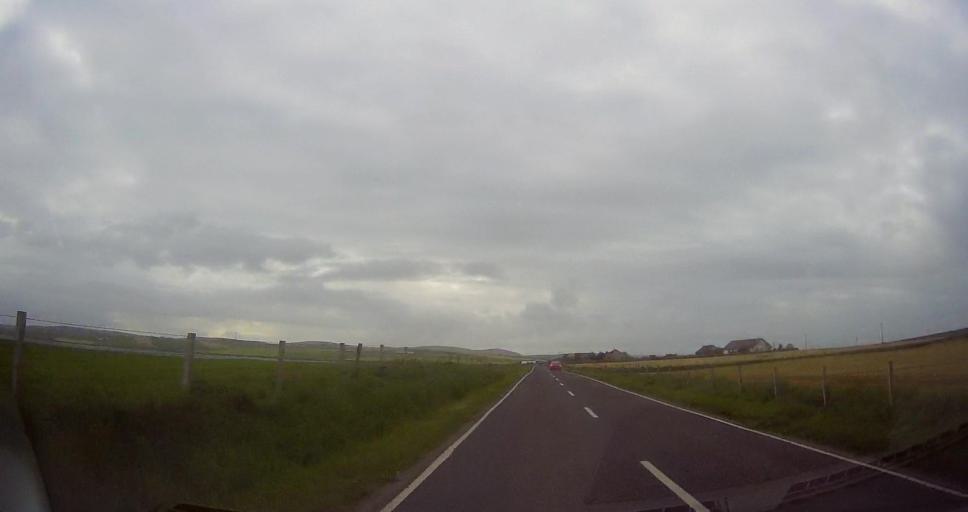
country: GB
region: Scotland
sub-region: Orkney Islands
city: Stromness
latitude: 58.9705
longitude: -3.2327
